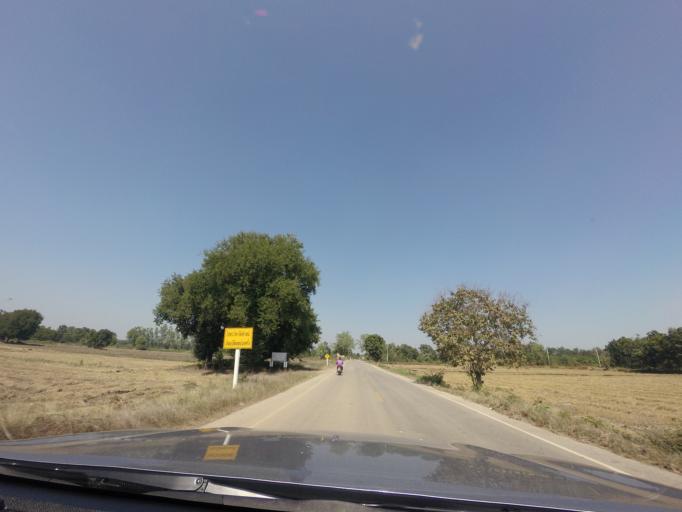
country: TH
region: Sukhothai
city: Si Samrong
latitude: 17.1480
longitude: 99.7696
